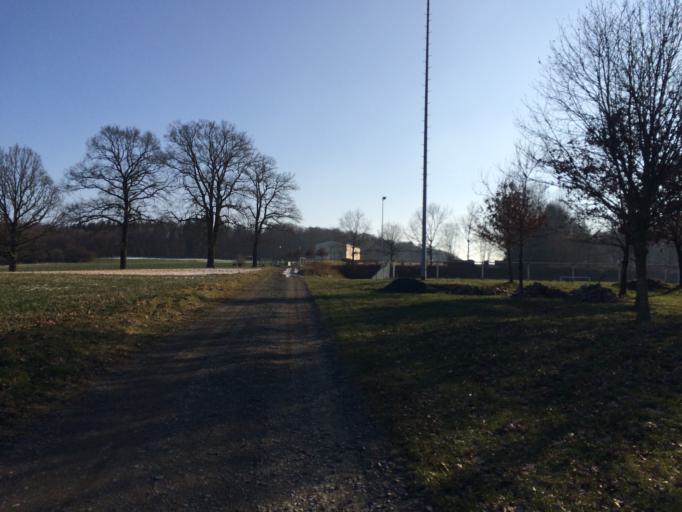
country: DE
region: Hesse
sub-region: Regierungsbezirk Giessen
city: Ebsdorfergrund
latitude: 50.7519
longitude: 8.8866
